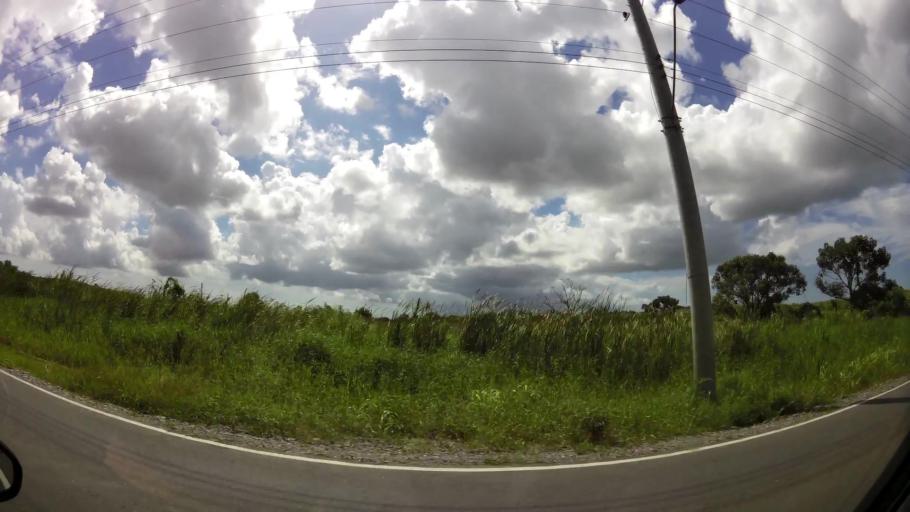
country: TT
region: Penal/Debe
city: Debe
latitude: 10.2310
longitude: -61.4929
